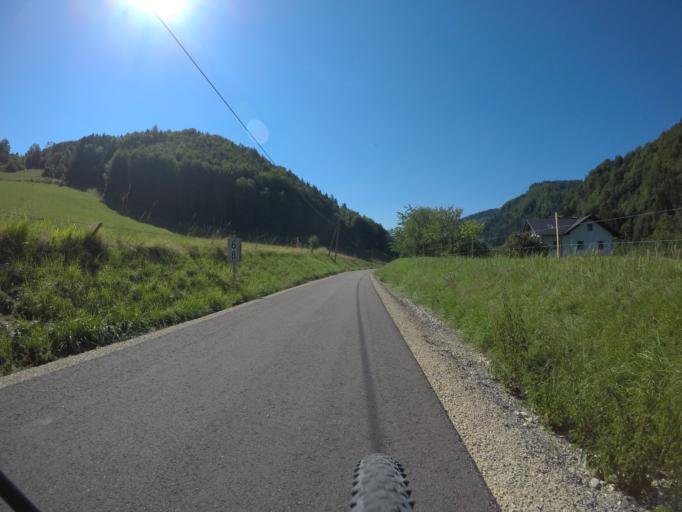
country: AT
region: Lower Austria
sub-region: Politischer Bezirk Amstetten
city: Ybbsitz
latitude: 47.9338
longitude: 14.8255
